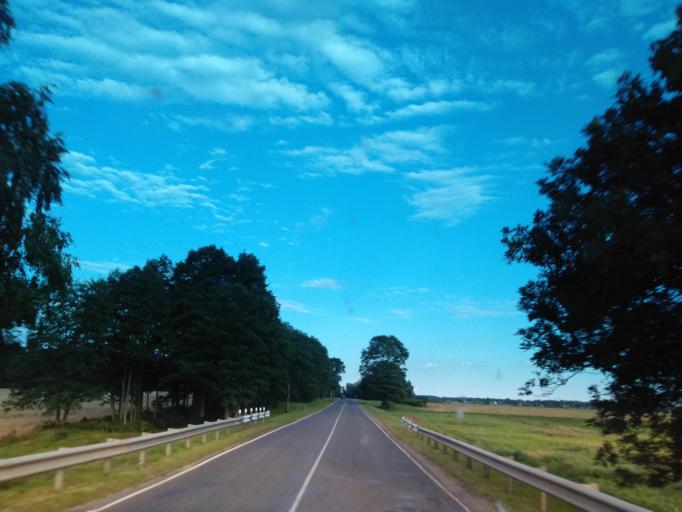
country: BY
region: Minsk
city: Uzda
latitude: 53.4438
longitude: 27.2821
